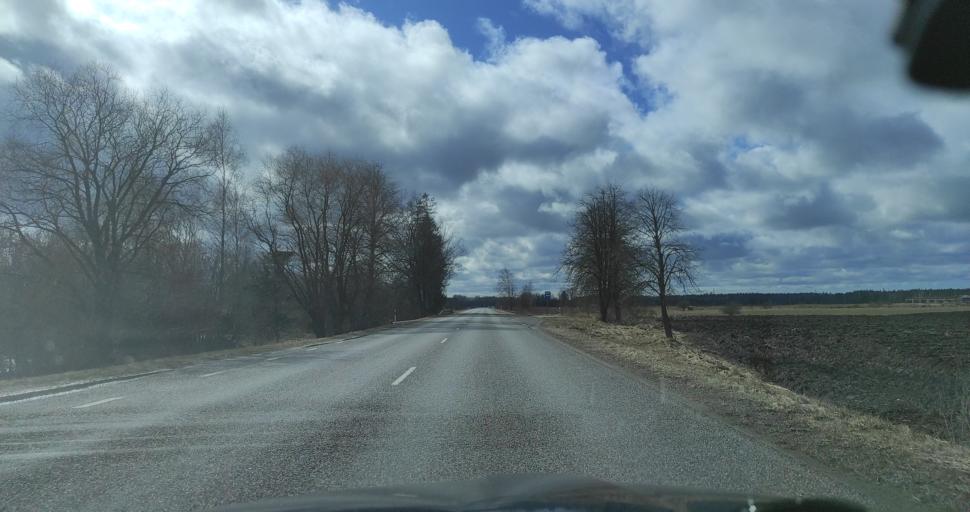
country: LV
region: Kuldigas Rajons
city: Kuldiga
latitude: 57.0033
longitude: 22.1383
